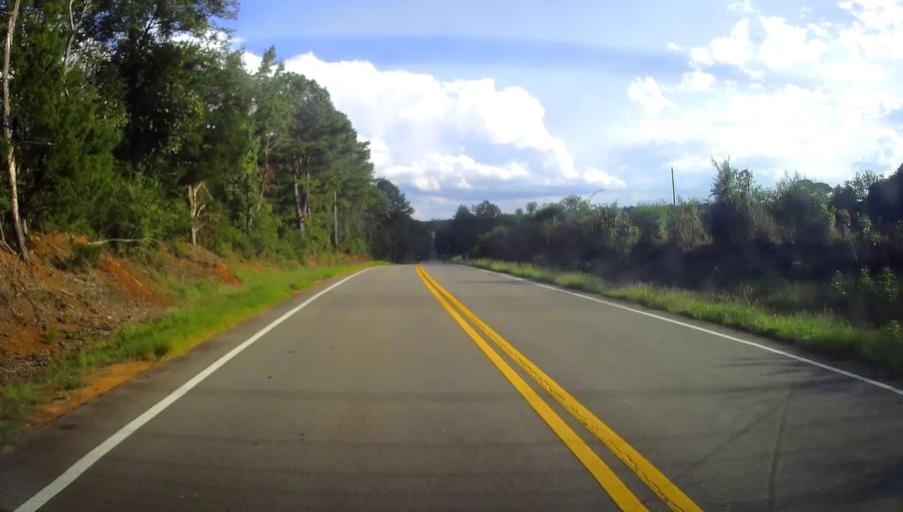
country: US
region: Georgia
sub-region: Monroe County
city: Forsyth
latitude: 32.9436
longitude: -83.9580
